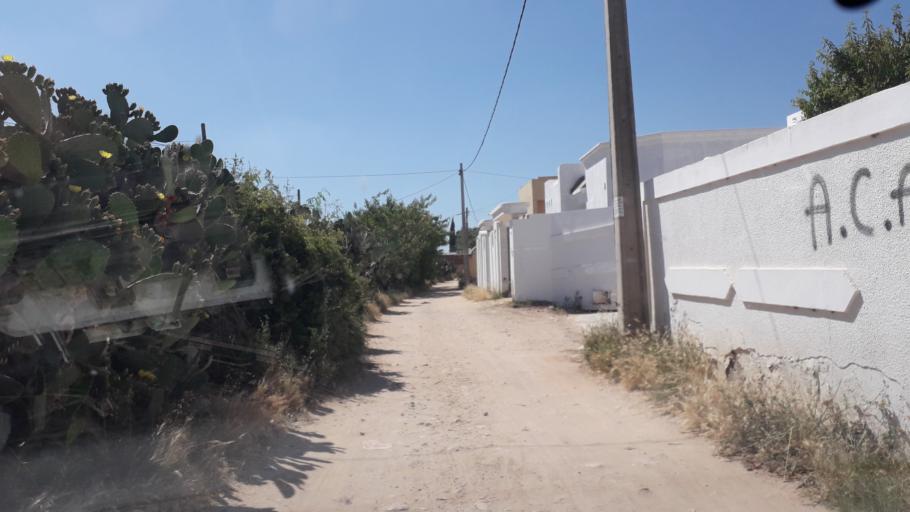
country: TN
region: Safaqis
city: Al Qarmadah
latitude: 34.8184
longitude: 10.7642
